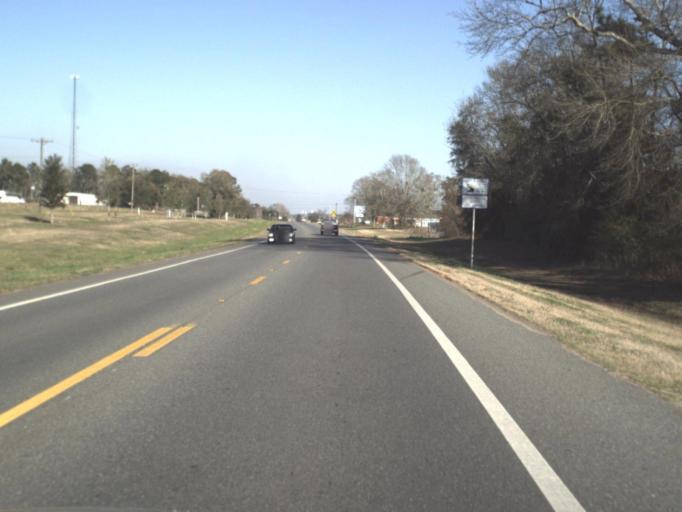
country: US
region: Florida
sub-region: Jackson County
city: Sneads
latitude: 30.7085
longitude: -84.9074
